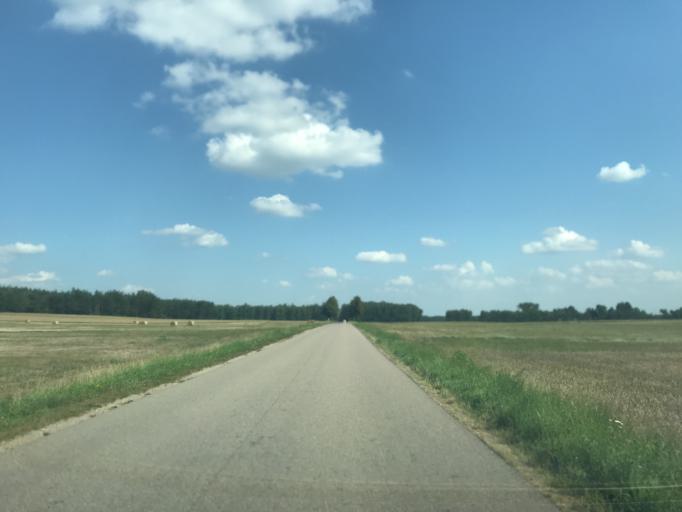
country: PL
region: Warmian-Masurian Voivodeship
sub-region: Powiat dzialdowski
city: Ilowo -Osada
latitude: 53.1119
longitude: 20.2684
